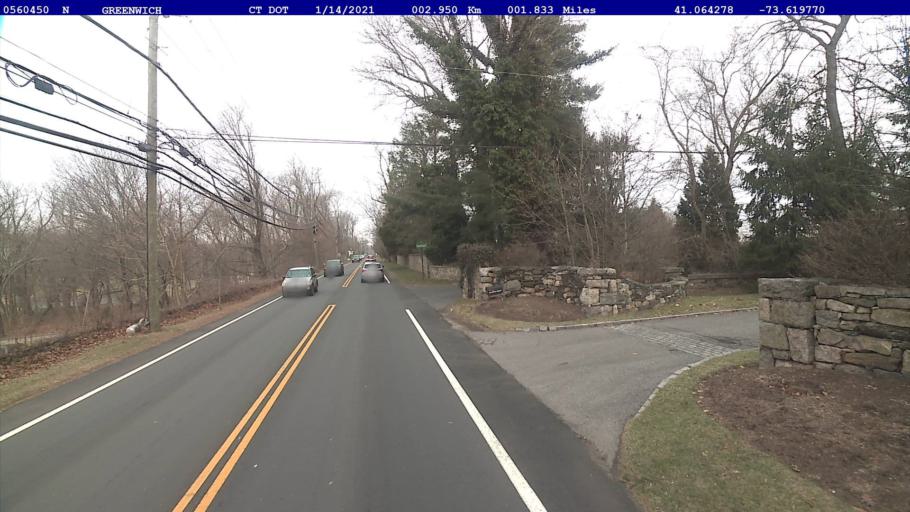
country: US
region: Connecticut
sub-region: Fairfield County
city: Cos Cob
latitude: 41.0643
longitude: -73.6198
